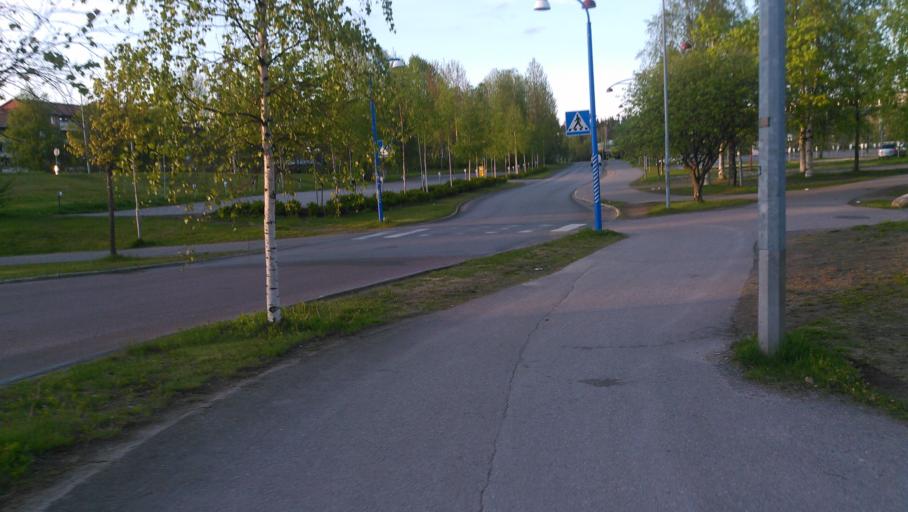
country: SE
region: Vaesterbotten
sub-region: Umea Kommun
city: Umea
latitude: 63.8219
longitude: 20.3013
